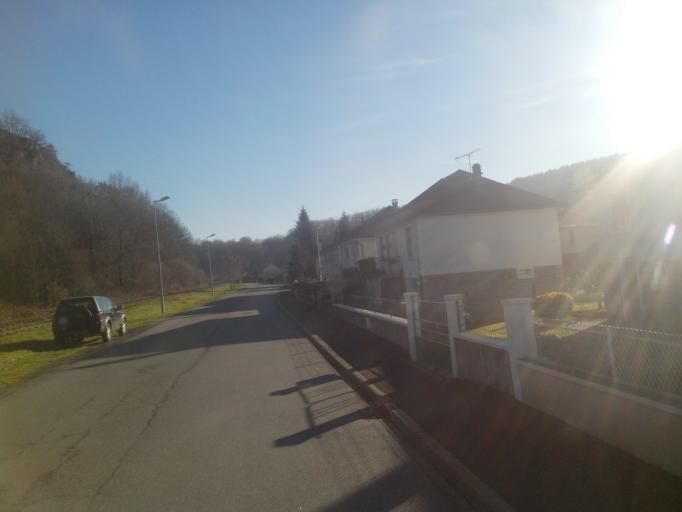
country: FR
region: Limousin
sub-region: Departement de la Correze
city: Bort-les-Orgues
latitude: 45.3882
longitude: 2.4972
